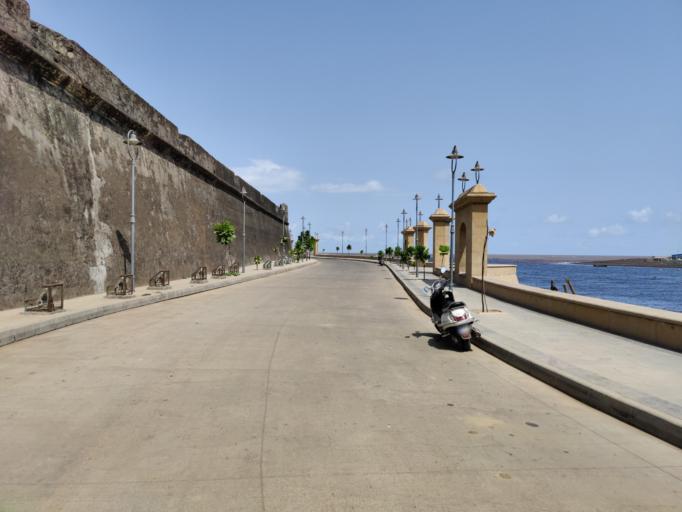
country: IN
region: Daman and Diu
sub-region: Daman District
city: Daman
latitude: 20.4103
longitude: 72.8320
